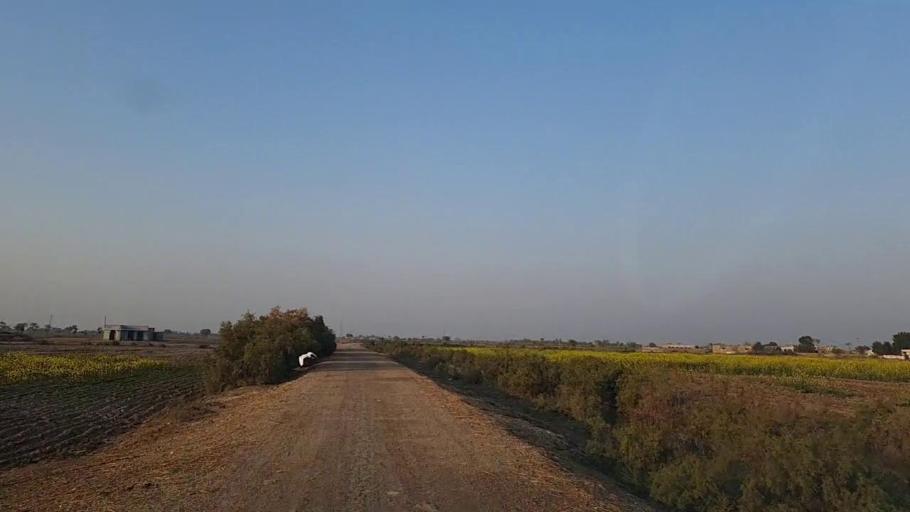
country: PK
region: Sindh
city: Bandhi
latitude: 26.5459
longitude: 68.3167
